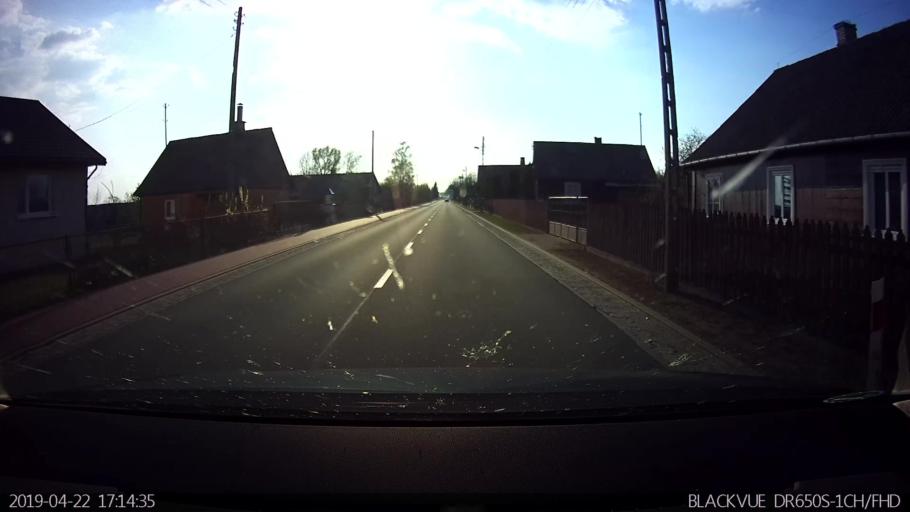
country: PL
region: Masovian Voivodeship
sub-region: Powiat sokolowski
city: Jablonna Lacka
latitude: 52.4015
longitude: 22.5007
